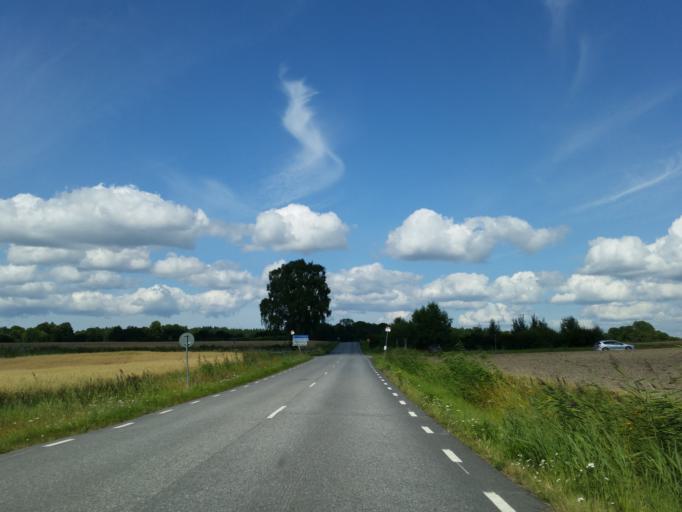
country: SE
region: Stockholm
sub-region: Sodertalje Kommun
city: Pershagen
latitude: 59.0443
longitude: 17.6741
